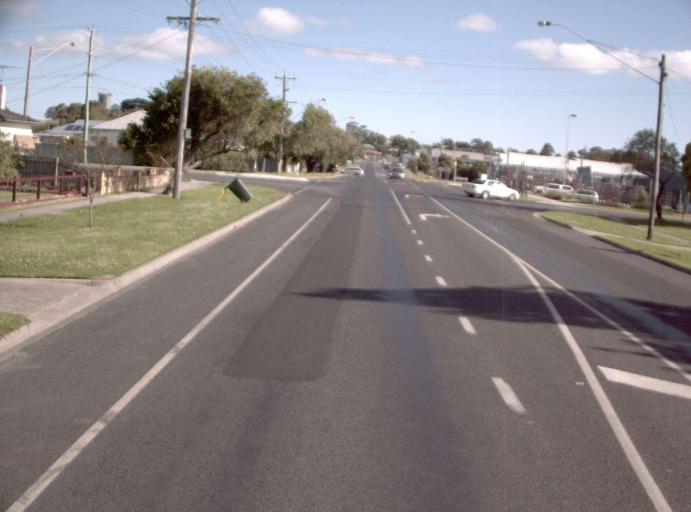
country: AU
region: Victoria
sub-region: Bass Coast
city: North Wonthaggi
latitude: -38.6018
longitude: 145.5931
